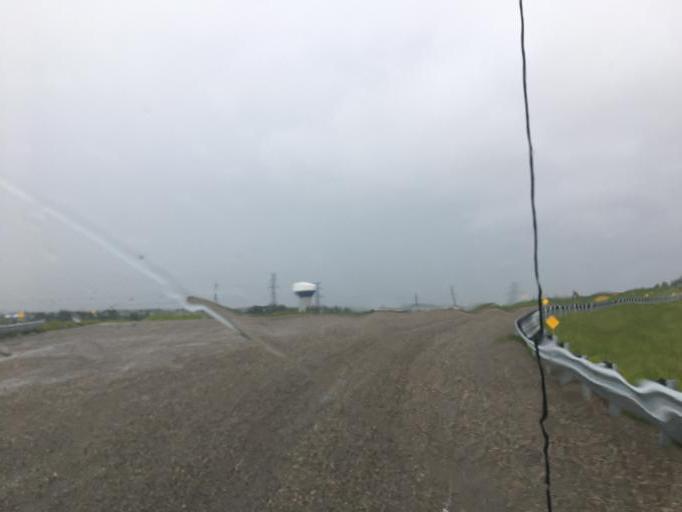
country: CA
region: Ontario
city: Waterloo
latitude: 43.4411
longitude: -80.5768
